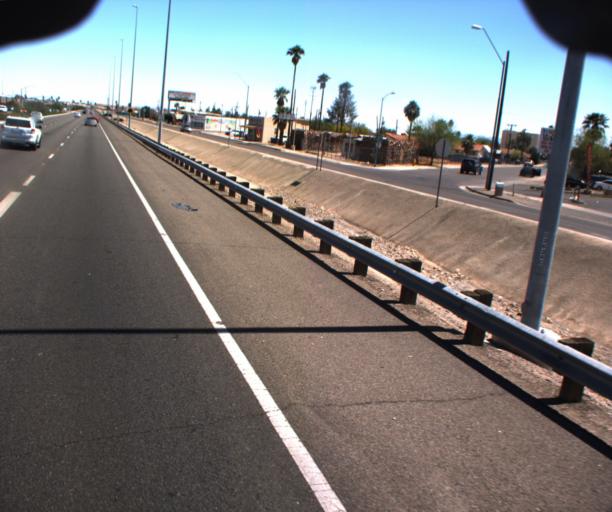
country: US
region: Arizona
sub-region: Maricopa County
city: El Mirage
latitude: 33.6179
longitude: -112.3237
